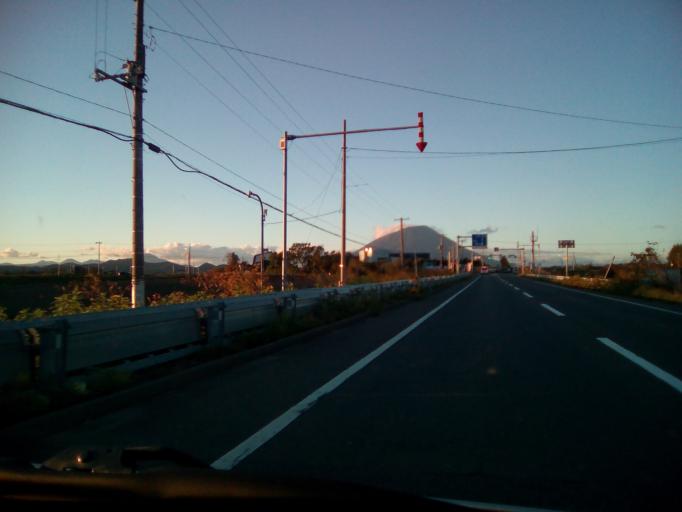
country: JP
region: Hokkaido
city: Niseko Town
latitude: 42.6608
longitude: 140.8119
